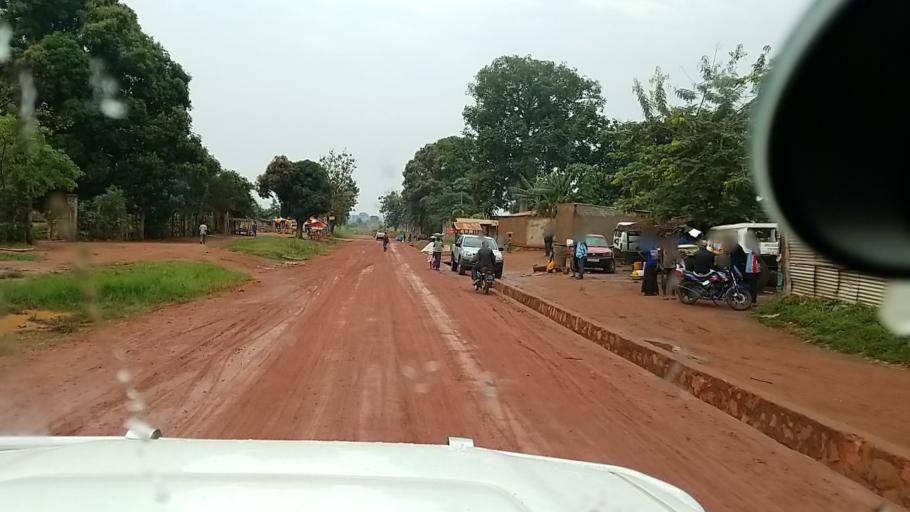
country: CD
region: Equateur
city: Gemena
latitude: 3.2375
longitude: 19.7800
